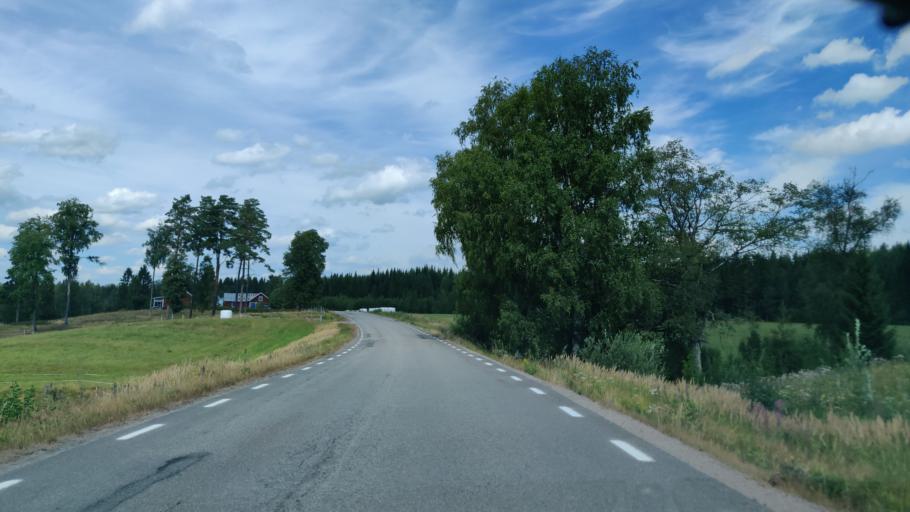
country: SE
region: Vaermland
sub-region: Hagfors Kommun
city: Ekshaerad
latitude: 60.0916
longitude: 13.5094
